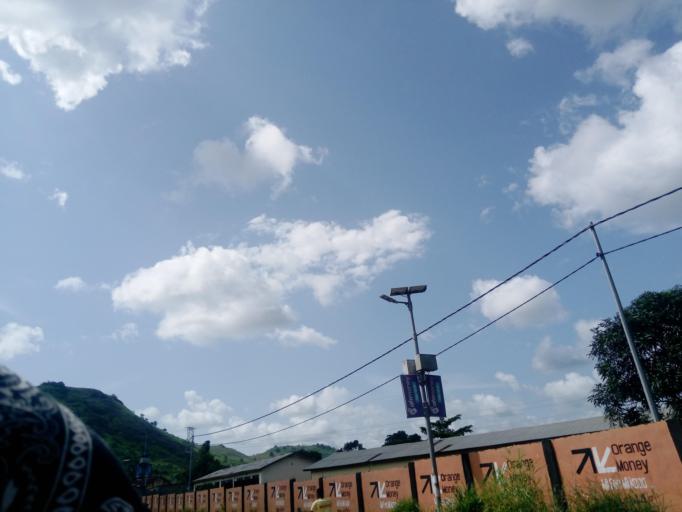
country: SL
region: Northern Province
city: Makeni
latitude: 8.8979
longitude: -12.0424
